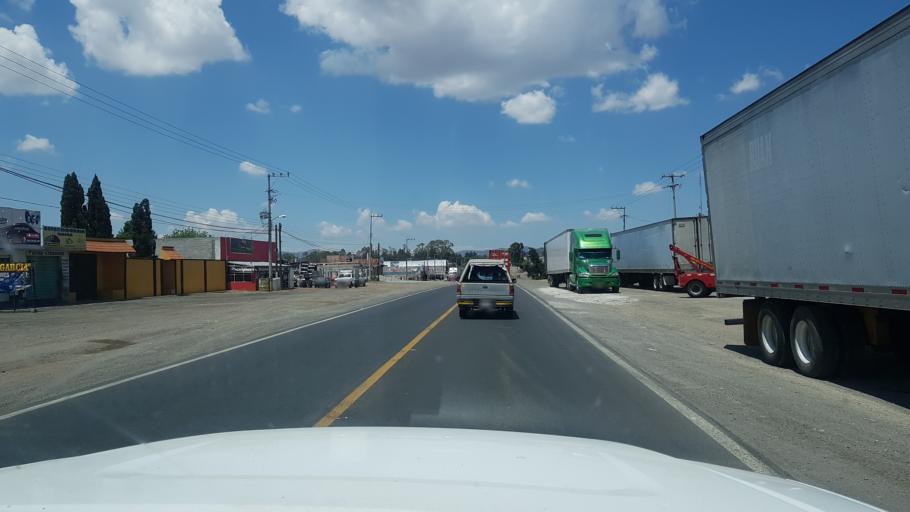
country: MX
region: Hidalgo
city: Calpulalpan
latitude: 19.5872
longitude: -98.5478
